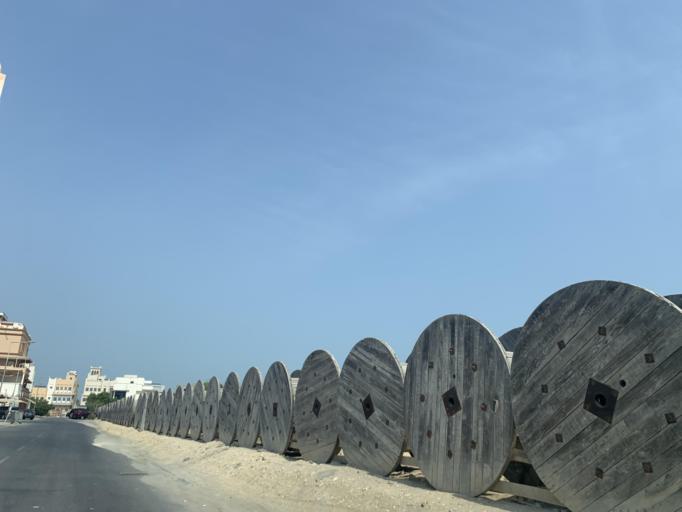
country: BH
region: Muharraq
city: Al Hadd
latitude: 26.2633
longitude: 50.6583
